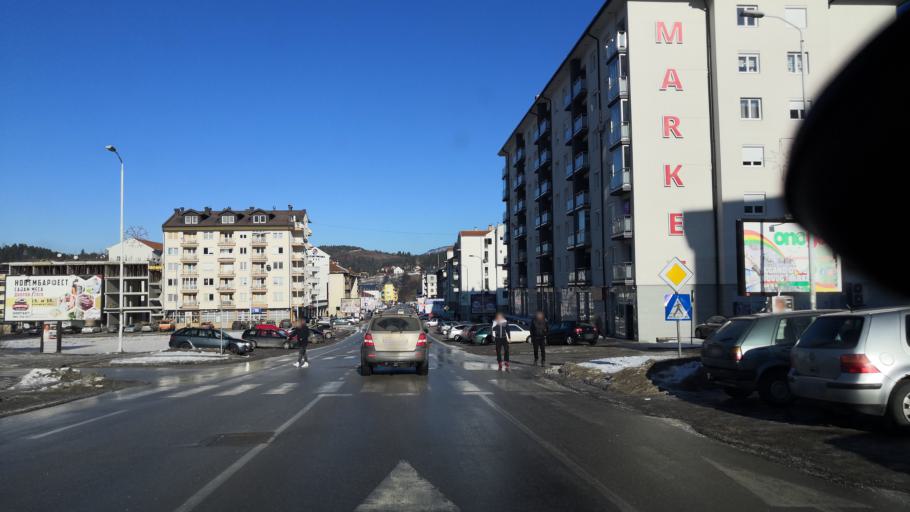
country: BA
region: Republika Srpska
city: Pale
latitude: 43.8139
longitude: 18.5665
